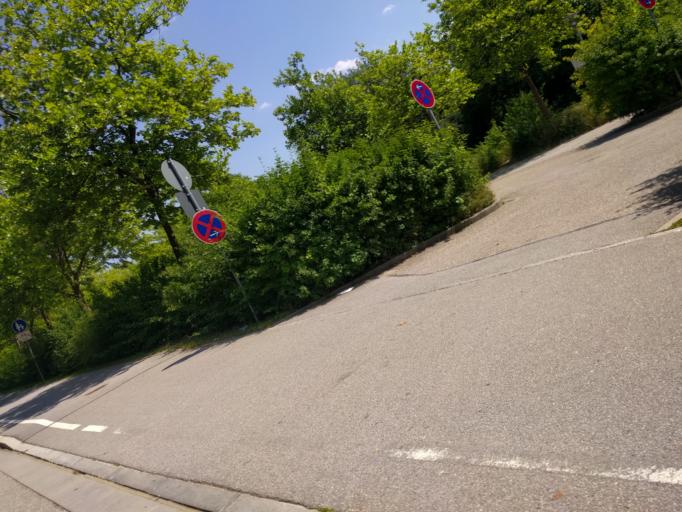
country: DE
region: Bavaria
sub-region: Upper Palatinate
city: Pentling
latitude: 48.9928
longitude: 12.0923
